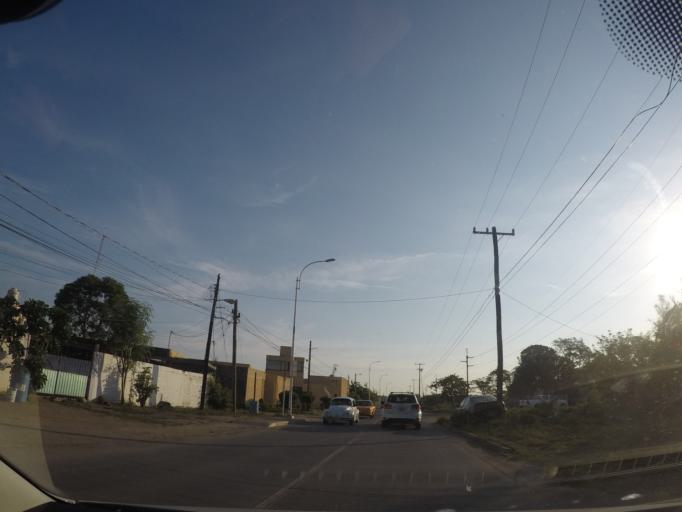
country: MX
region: Oaxaca
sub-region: Salina Cruz
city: Salina Cruz
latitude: 16.2143
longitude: -95.1928
